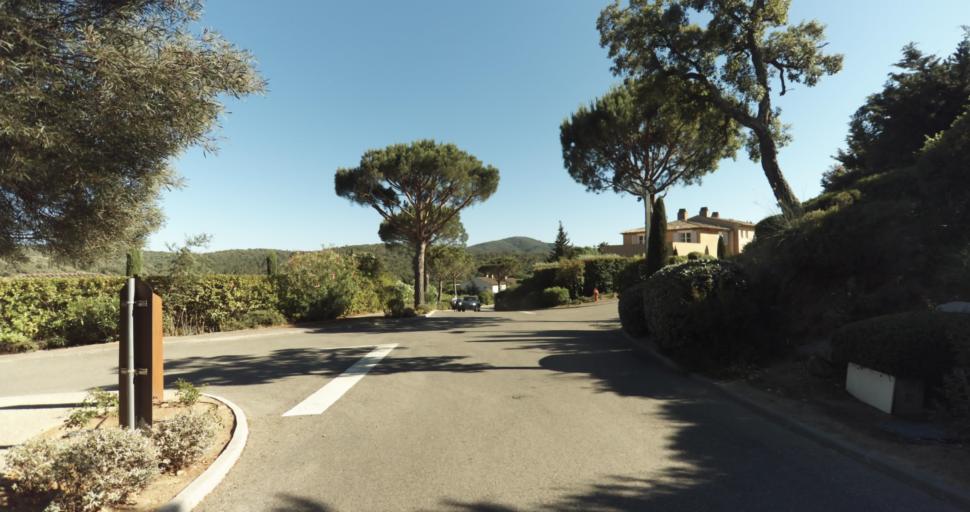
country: FR
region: Provence-Alpes-Cote d'Azur
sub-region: Departement du Var
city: Gassin
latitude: 43.2560
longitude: 6.6048
